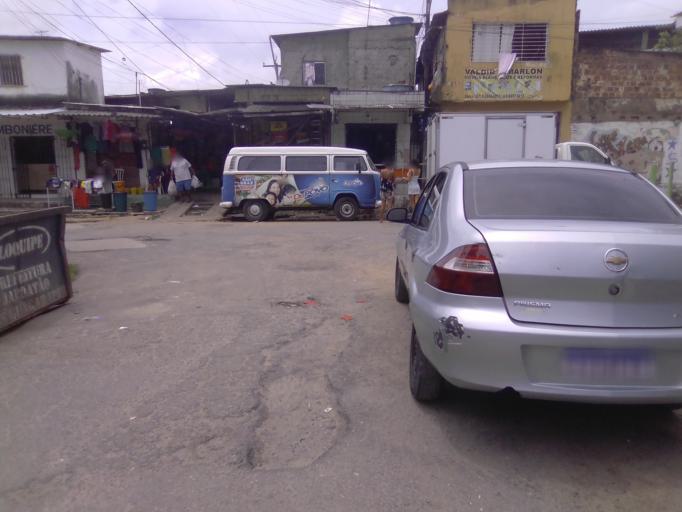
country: BR
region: Pernambuco
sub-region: Jaboatao Dos Guararapes
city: Jaboatao dos Guararapes
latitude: -8.0689
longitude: -34.9953
